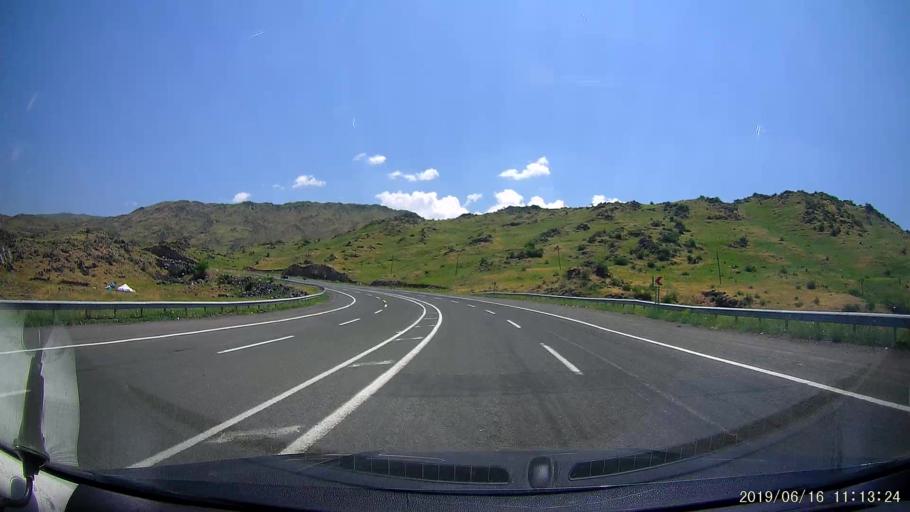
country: TR
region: Igdir
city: Igdir
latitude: 39.7843
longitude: 44.1372
